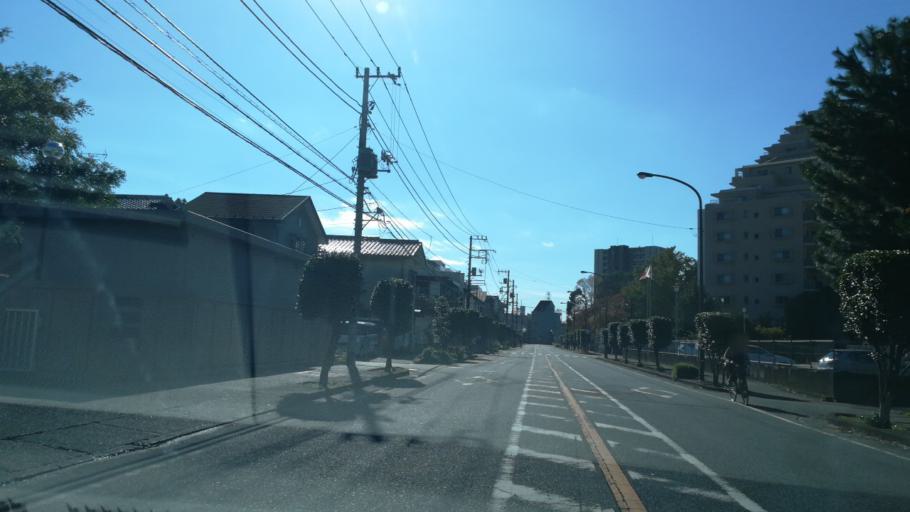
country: JP
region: Tokyo
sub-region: Machida-shi
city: Machida
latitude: 35.5752
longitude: 139.3876
